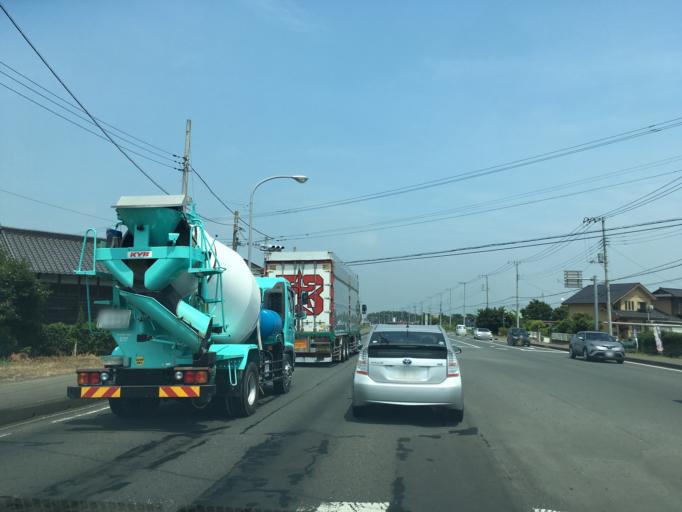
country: JP
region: Ibaraki
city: Hitachi-Naka
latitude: 36.3895
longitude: 140.5794
